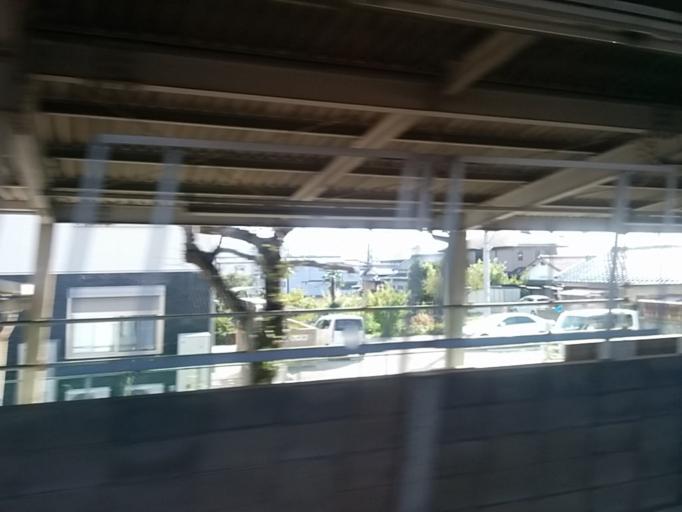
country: JP
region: Kyoto
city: Tanabe
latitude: 34.7806
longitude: 135.7894
